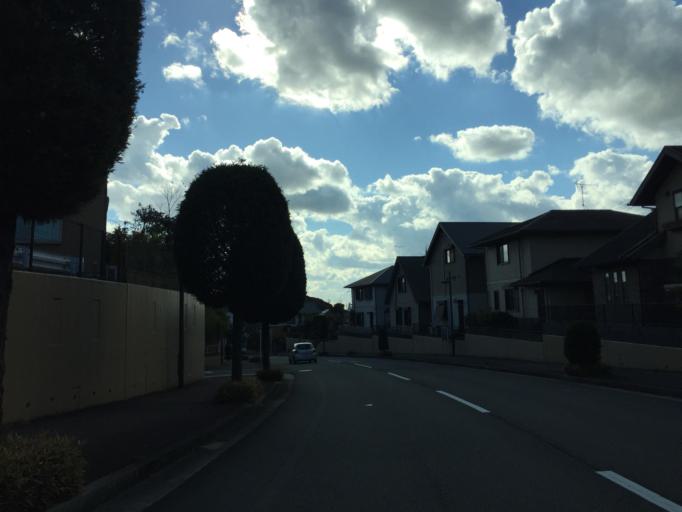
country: JP
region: Wakayama
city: Wakayama-shi
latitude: 34.2706
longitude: 135.1483
